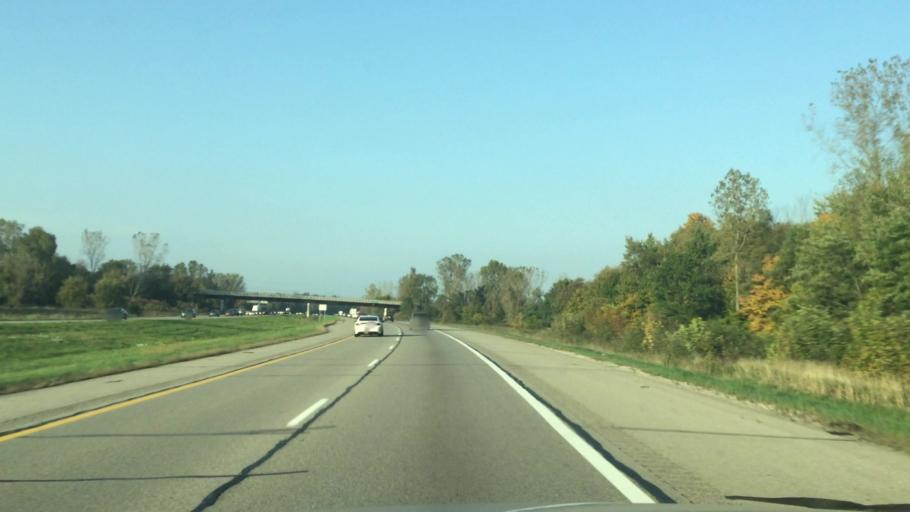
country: US
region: Michigan
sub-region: Washtenaw County
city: Ypsilanti
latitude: 42.3449
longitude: -83.5958
